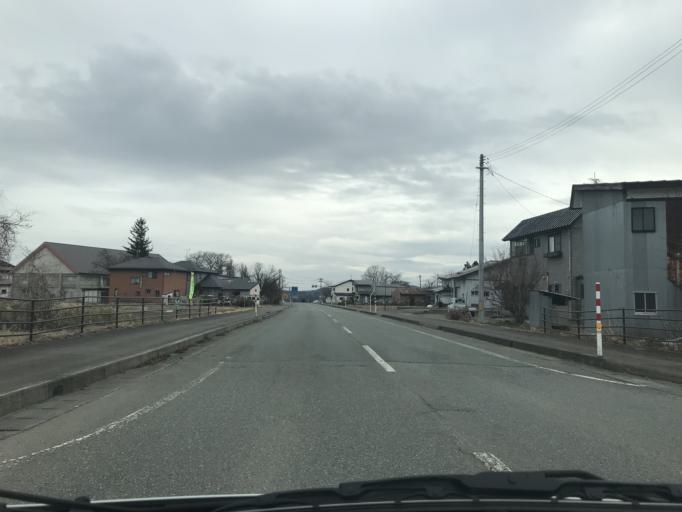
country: JP
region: Iwate
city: Kitakami
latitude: 39.3135
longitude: 140.9757
